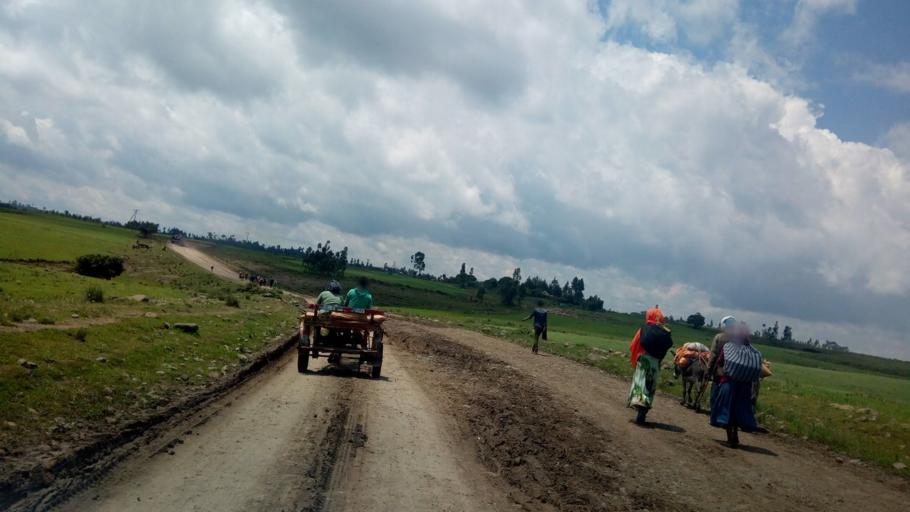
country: ET
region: Oromiya
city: Sendafa
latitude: 8.9873
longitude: 39.1255
